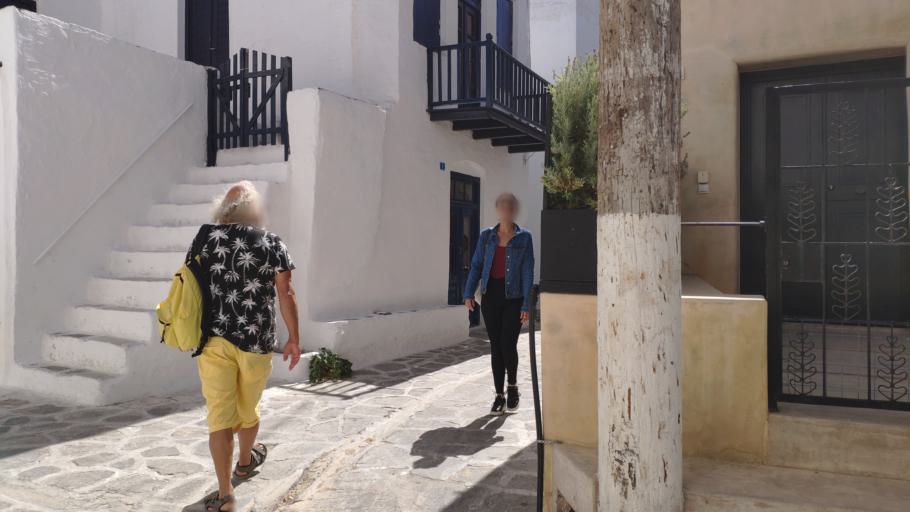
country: GR
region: South Aegean
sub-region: Nomos Kykladon
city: Paros
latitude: 37.0830
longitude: 25.1473
